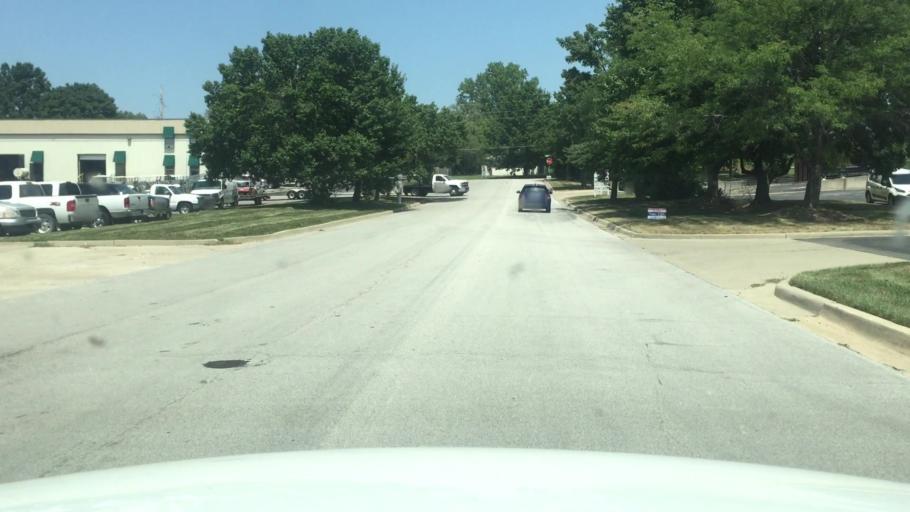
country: US
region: Missouri
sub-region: Jackson County
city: Blue Springs
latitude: 38.9884
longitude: -94.3520
